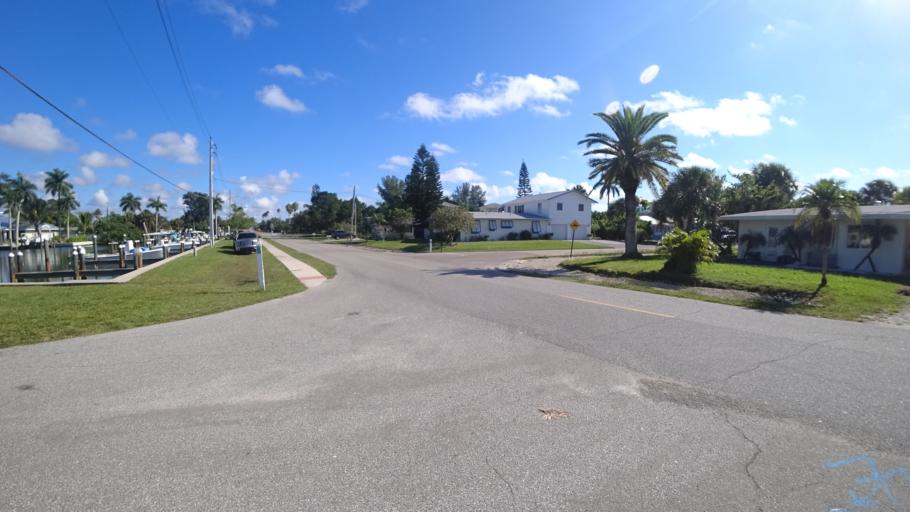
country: US
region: Florida
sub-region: Manatee County
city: Anna Maria
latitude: 27.5195
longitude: -82.7234
